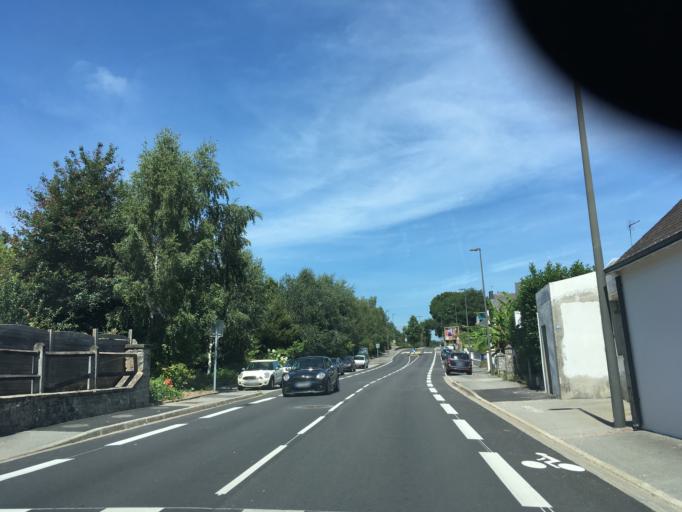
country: FR
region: Brittany
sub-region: Departement du Finistere
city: Quimper
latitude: 48.0088
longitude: -4.1196
